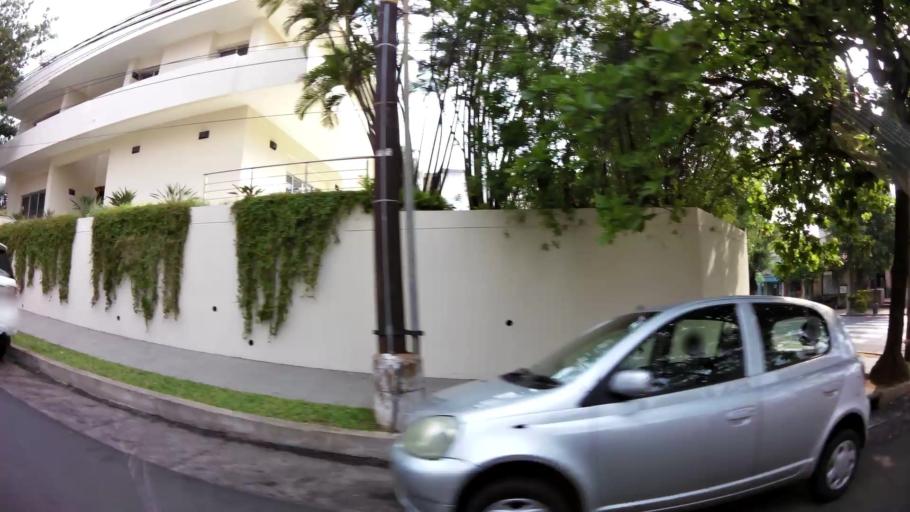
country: PY
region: Asuncion
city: Asuncion
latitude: -25.2877
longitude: -57.6176
